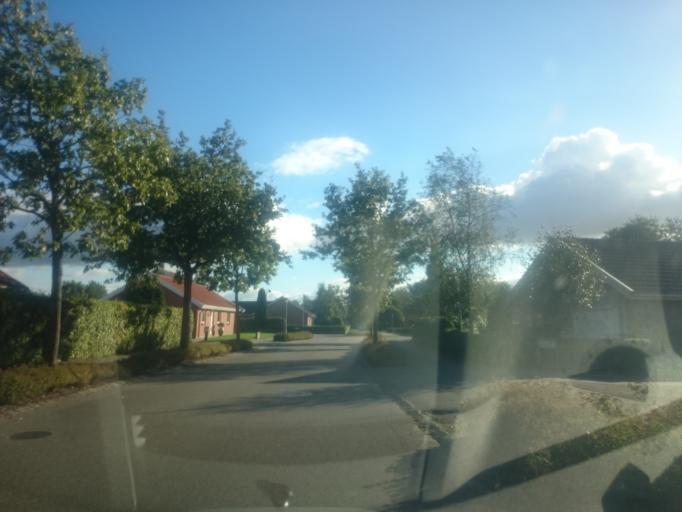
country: DK
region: South Denmark
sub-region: Billund Kommune
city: Billund
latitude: 55.7160
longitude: 9.1184
